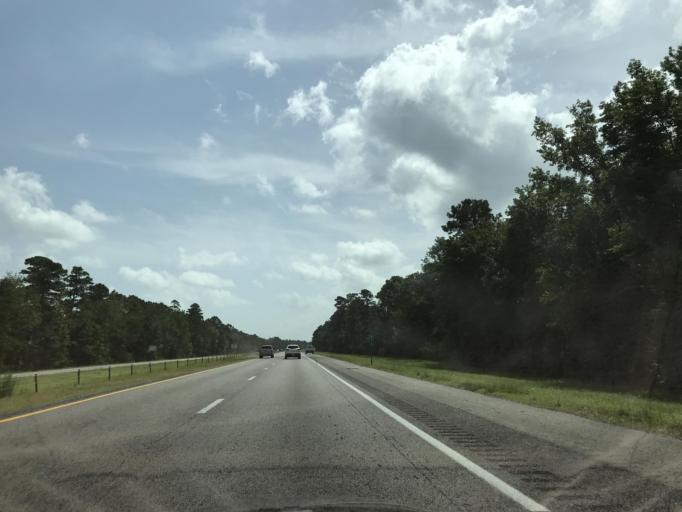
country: US
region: North Carolina
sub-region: Pender County
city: Rocky Point
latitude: 34.3995
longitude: -77.8732
